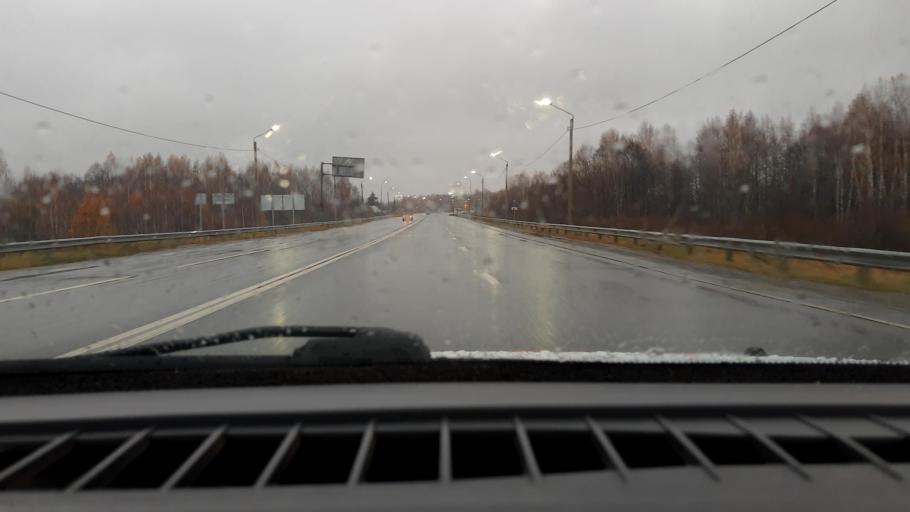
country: RU
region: Nizjnij Novgorod
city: Sitniki
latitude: 56.5032
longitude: 44.0246
